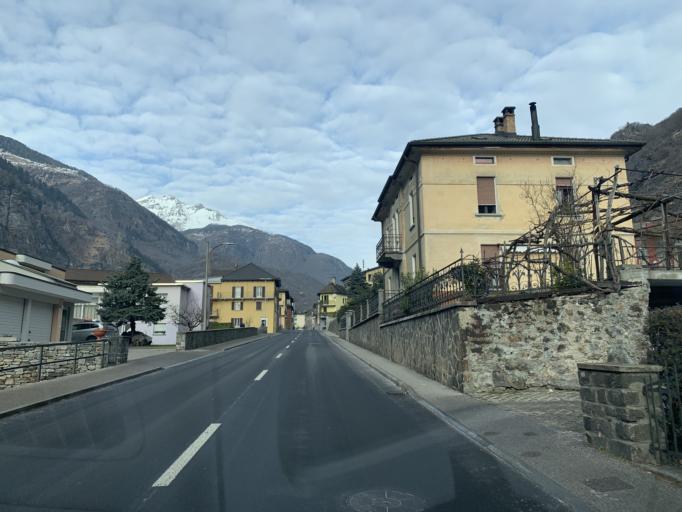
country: CH
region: Ticino
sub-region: Leventina District
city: Bodio
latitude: 46.4010
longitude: 8.8788
